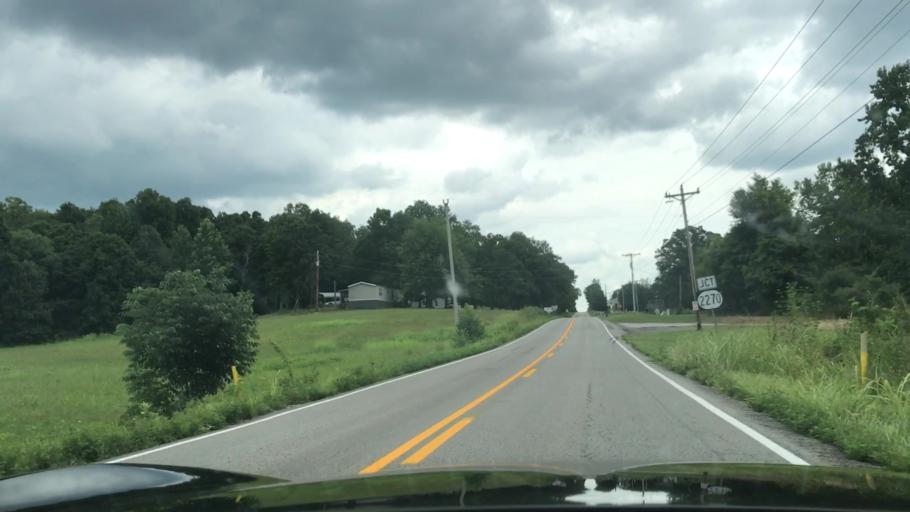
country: US
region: Kentucky
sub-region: Muhlenberg County
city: Central City
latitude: 37.1988
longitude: -86.9745
